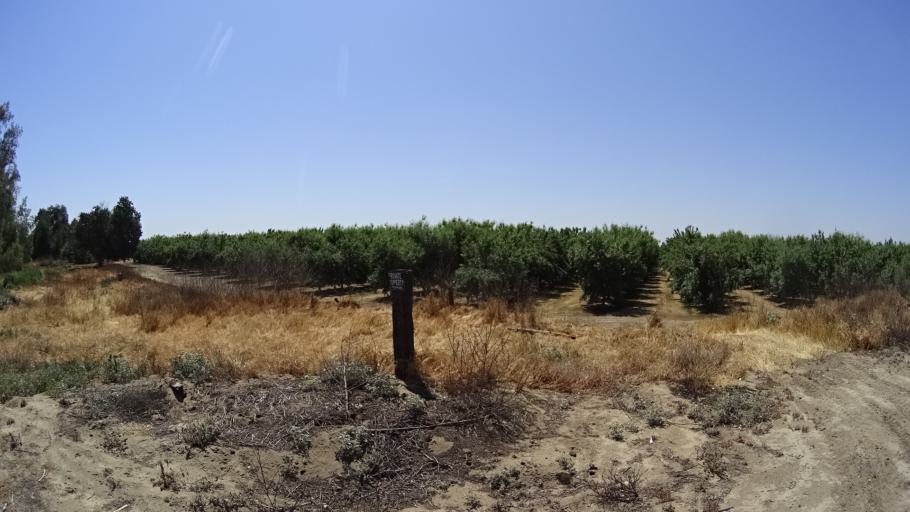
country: US
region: California
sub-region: Kings County
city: Lemoore
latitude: 36.3651
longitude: -119.8048
